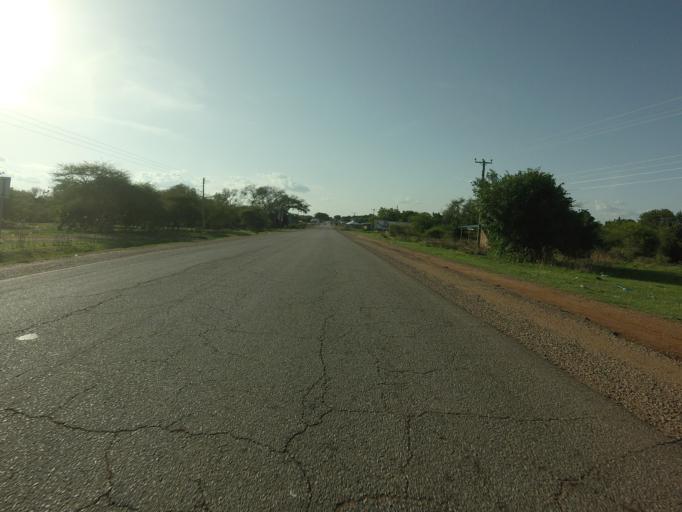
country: GH
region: Upper East
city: Navrongo
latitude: 10.9589
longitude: -1.0983
